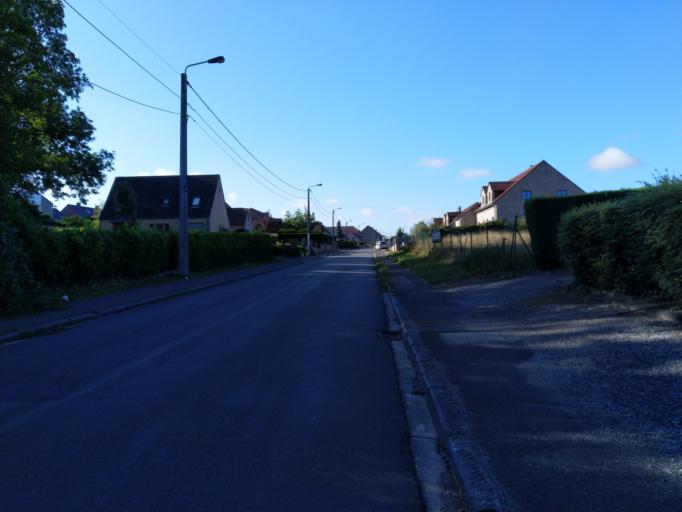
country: BE
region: Wallonia
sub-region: Province du Hainaut
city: Estinnes-au-Val
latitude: 50.4477
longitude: 4.0994
